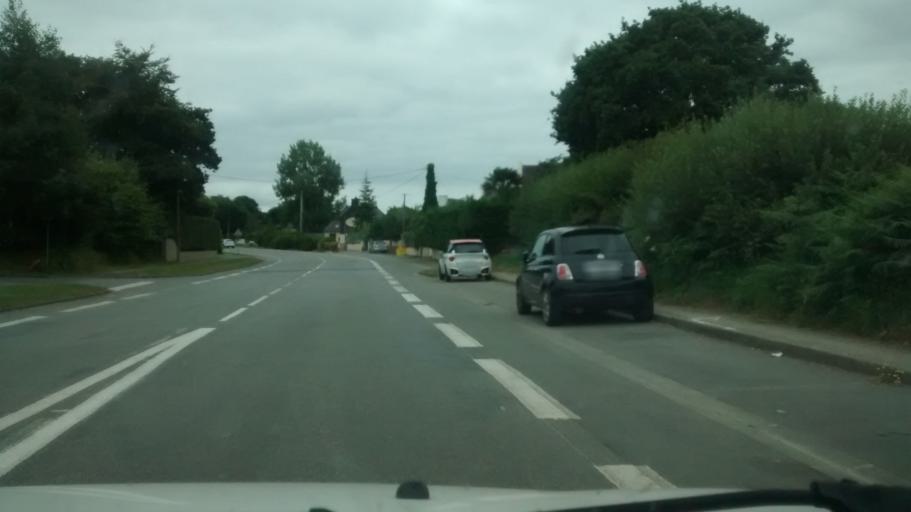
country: FR
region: Brittany
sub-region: Departement du Finistere
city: Plougastel-Daoulas
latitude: 48.3673
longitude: -4.3724
